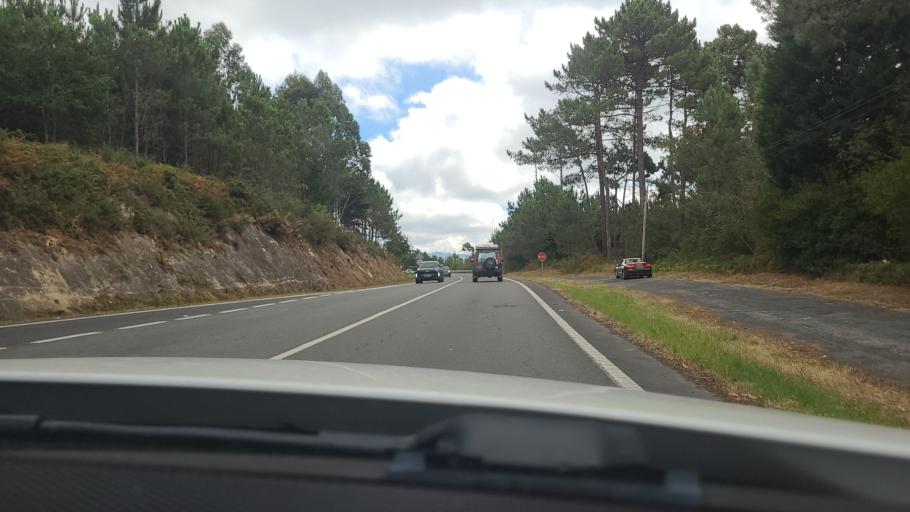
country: ES
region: Galicia
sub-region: Provincia da Coruna
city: Fisterra
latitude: 42.9281
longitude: -9.2509
